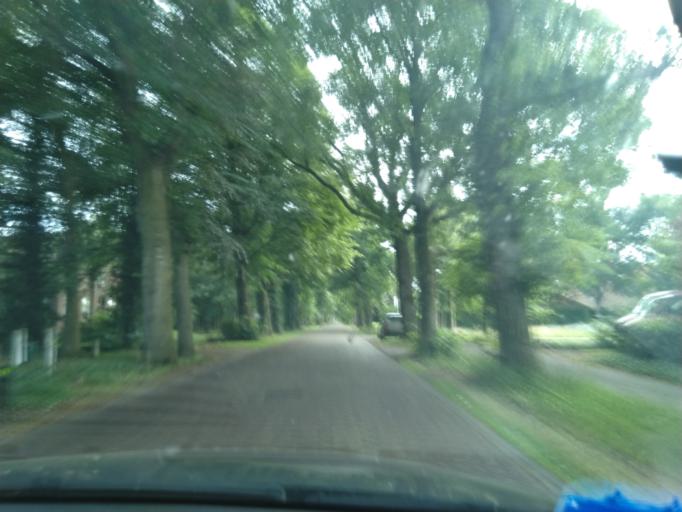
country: NL
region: Groningen
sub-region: Gemeente Vlagtwedde
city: Vlagtwedde
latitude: 53.0894
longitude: 7.1371
